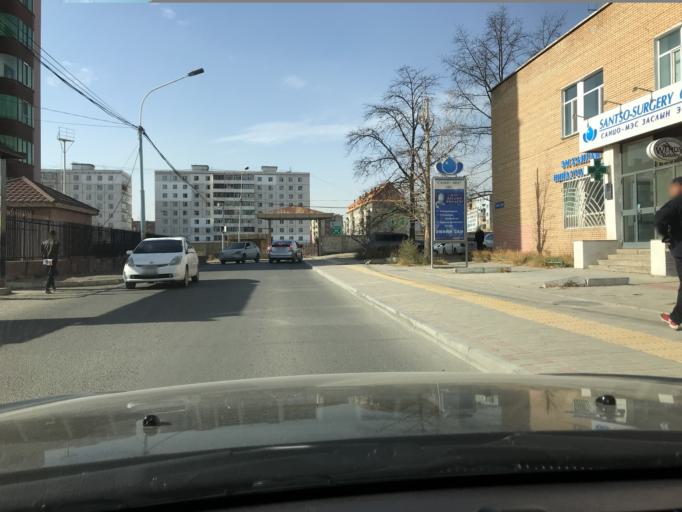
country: MN
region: Ulaanbaatar
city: Ulaanbaatar
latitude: 47.9215
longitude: 106.9509
